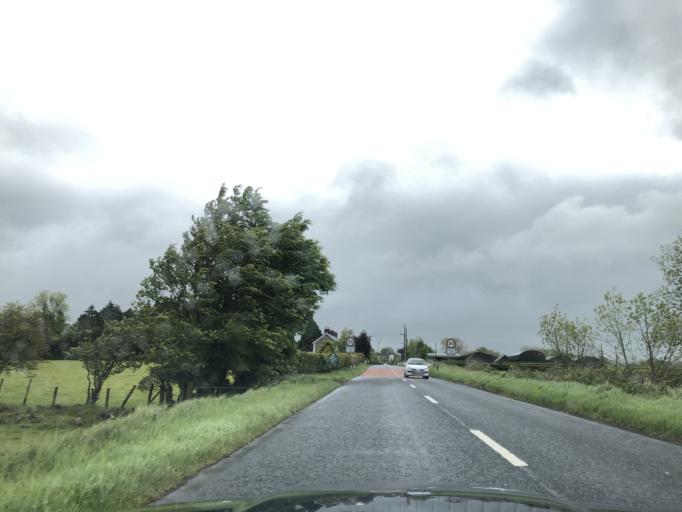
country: GB
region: Northern Ireland
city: Bushmills
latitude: 55.1536
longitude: -6.4163
